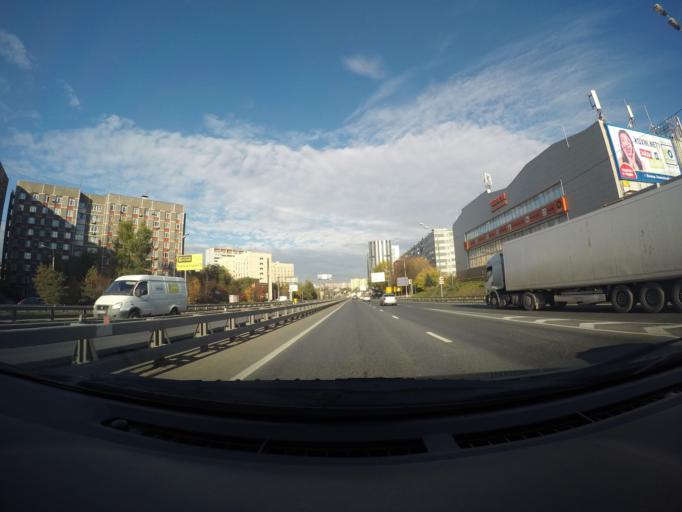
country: RU
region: Moskovskaya
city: Druzhba
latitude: 55.9127
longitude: 37.7750
